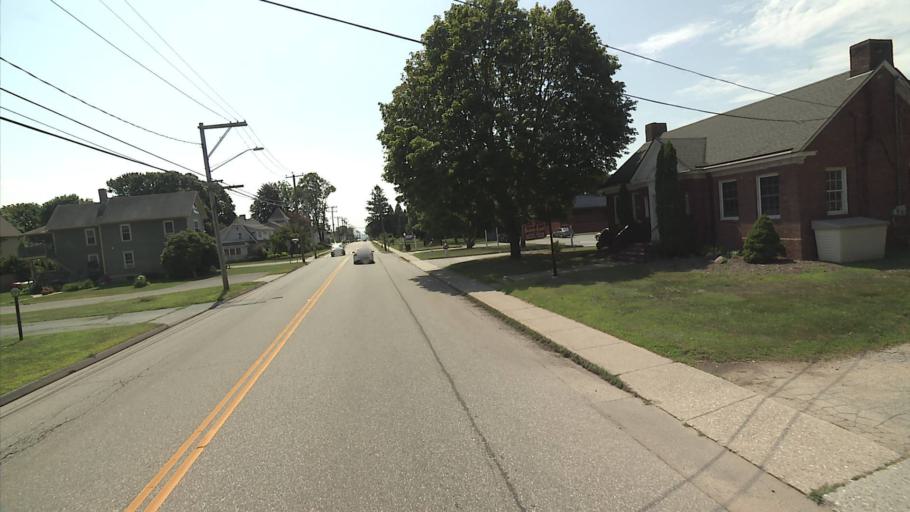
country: US
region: Connecticut
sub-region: New London County
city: Niantic
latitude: 41.3284
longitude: -72.1944
